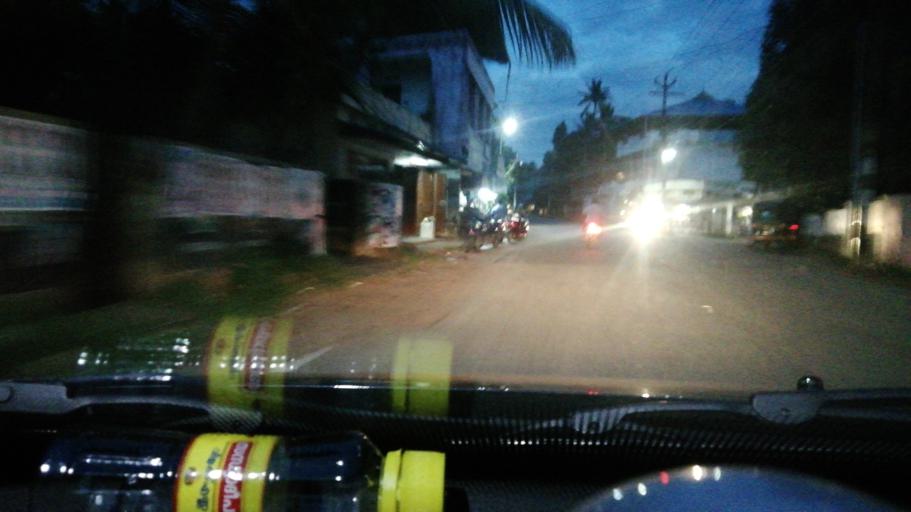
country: IN
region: Kerala
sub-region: Thiruvananthapuram
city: Paravur
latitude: 8.8122
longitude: 76.6811
